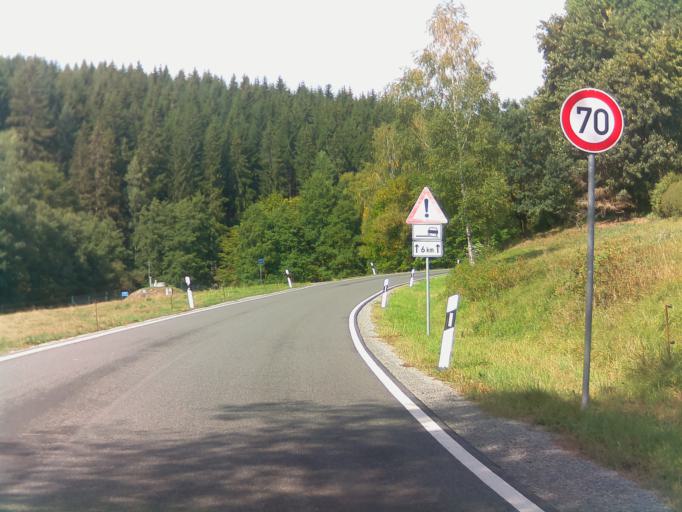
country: DE
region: Thuringia
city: Schwarza
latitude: 50.6293
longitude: 10.5314
